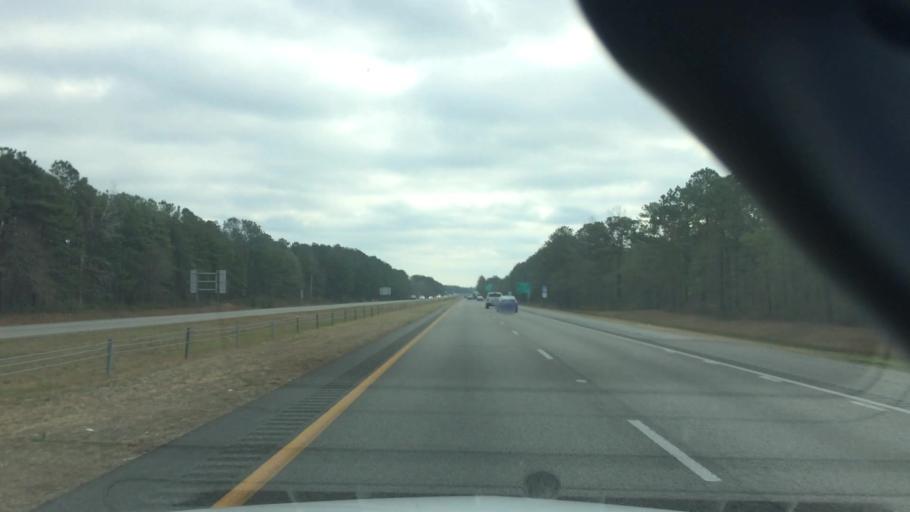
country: US
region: North Carolina
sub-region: New Hanover County
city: Skippers Corner
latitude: 34.3456
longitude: -77.8816
